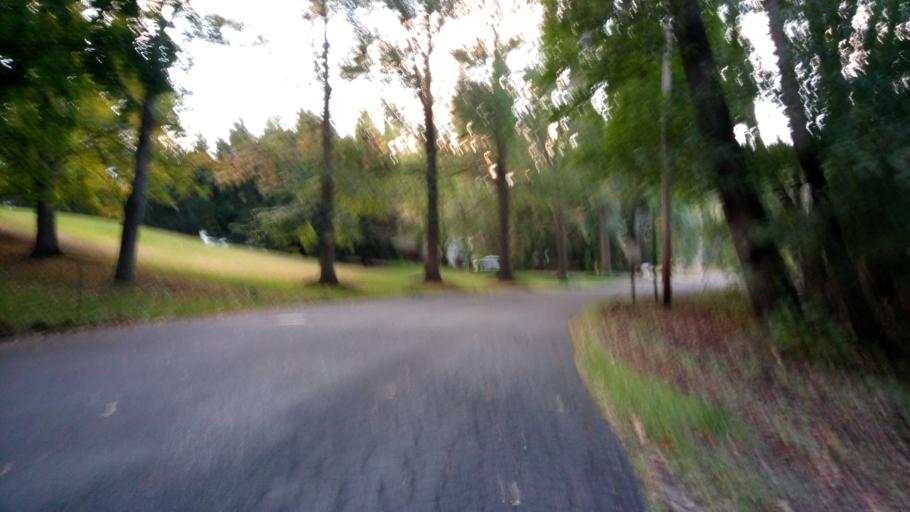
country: US
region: New York
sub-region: Chemung County
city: West Elmira
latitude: 42.0900
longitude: -76.8323
